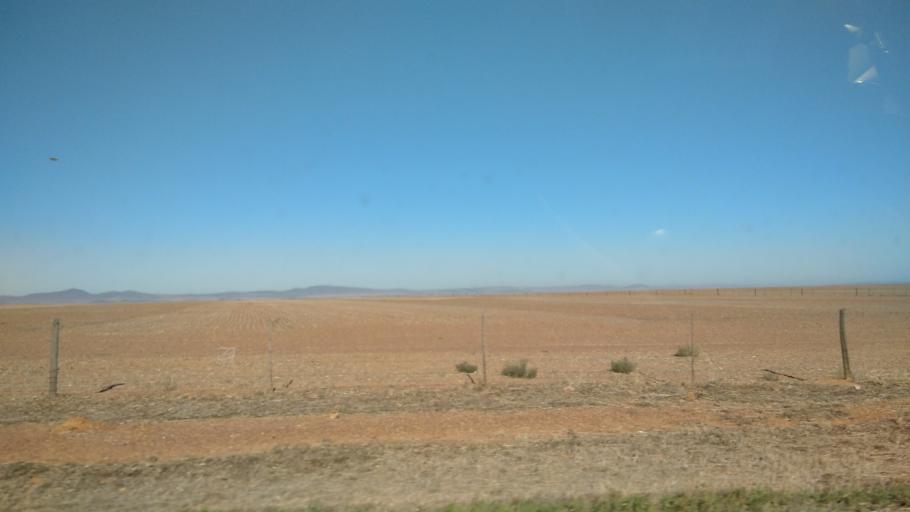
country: ZA
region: Western Cape
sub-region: West Coast District Municipality
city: Moorreesburg
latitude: -33.3126
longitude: 18.6210
